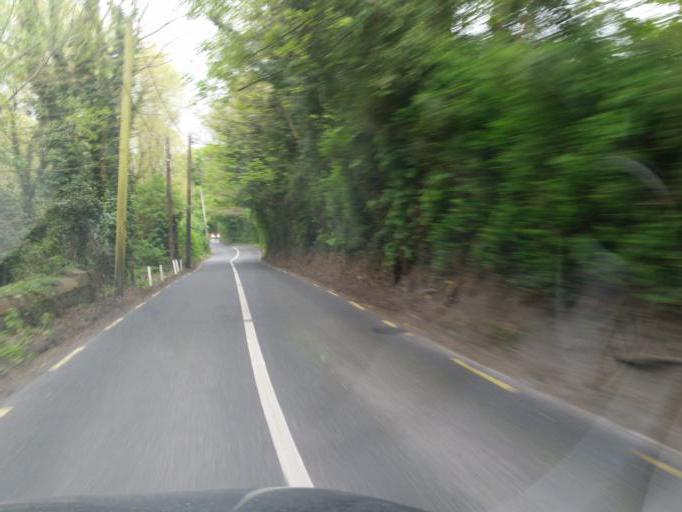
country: IE
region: Leinster
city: Castleknock
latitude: 53.3789
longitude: -6.3403
